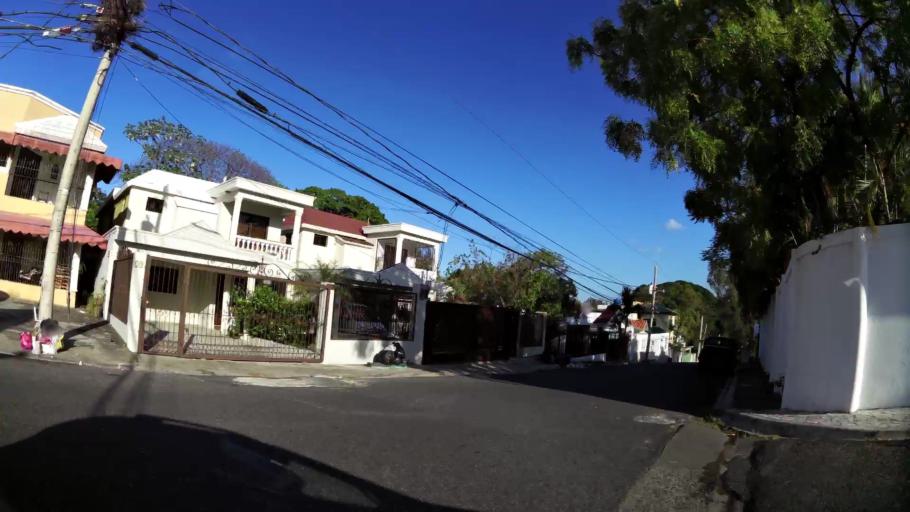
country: DO
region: Nacional
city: Santo Domingo
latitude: 18.4915
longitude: -69.9705
